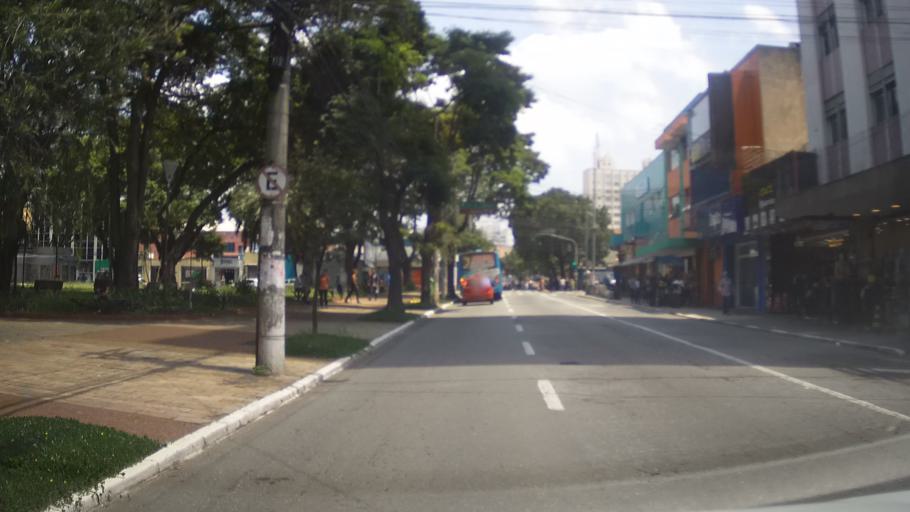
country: BR
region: Sao Paulo
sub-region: Guarulhos
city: Guarulhos
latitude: -23.4658
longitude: -46.5319
